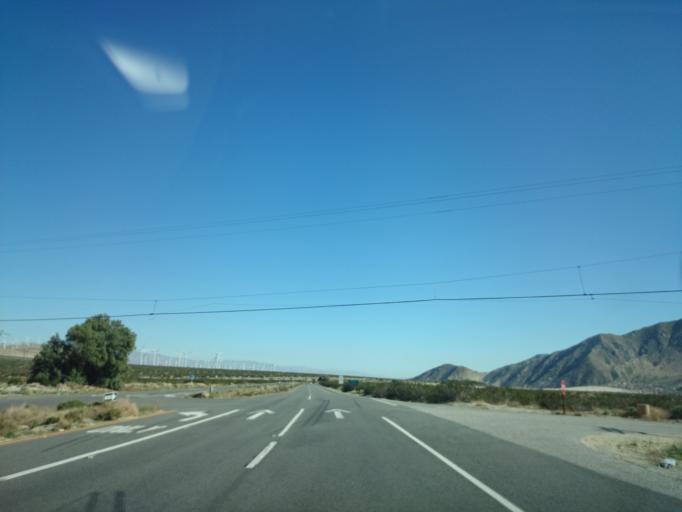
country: US
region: California
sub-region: Riverside County
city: Cabazon
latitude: 33.9141
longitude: -116.6680
